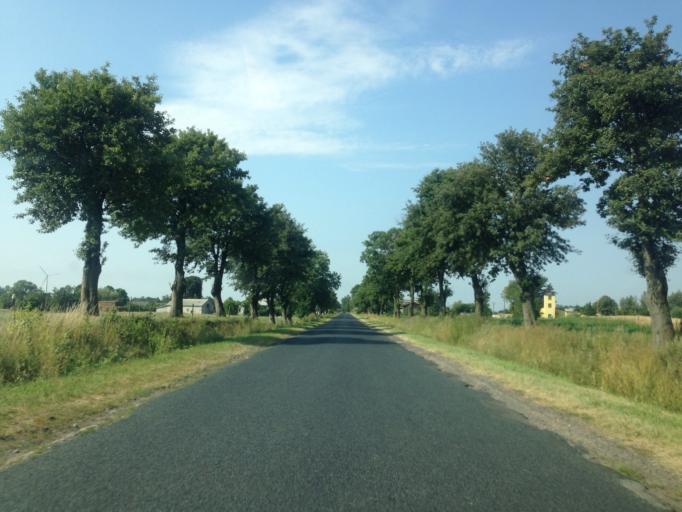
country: PL
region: Kujawsko-Pomorskie
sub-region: Powiat rypinski
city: Rypin
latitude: 53.1023
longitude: 19.4561
